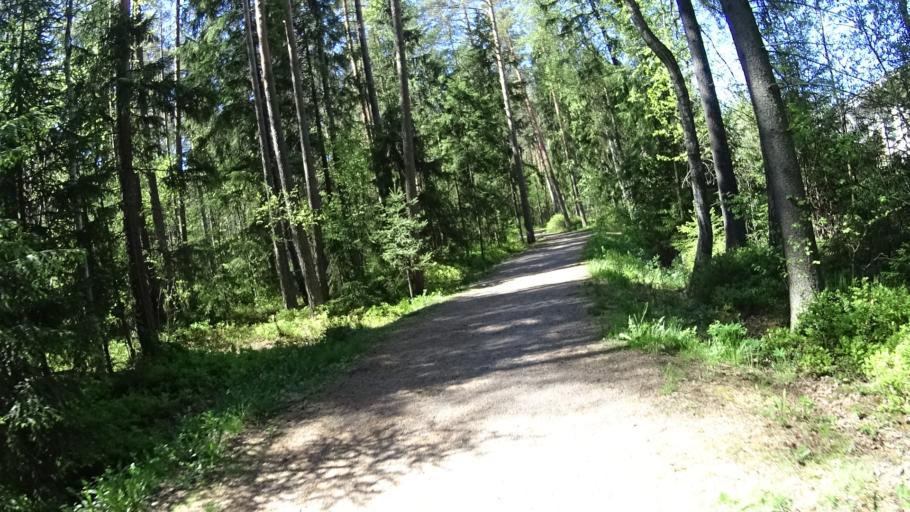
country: FI
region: Uusimaa
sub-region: Helsinki
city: Espoo
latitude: 60.2118
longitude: 24.6286
